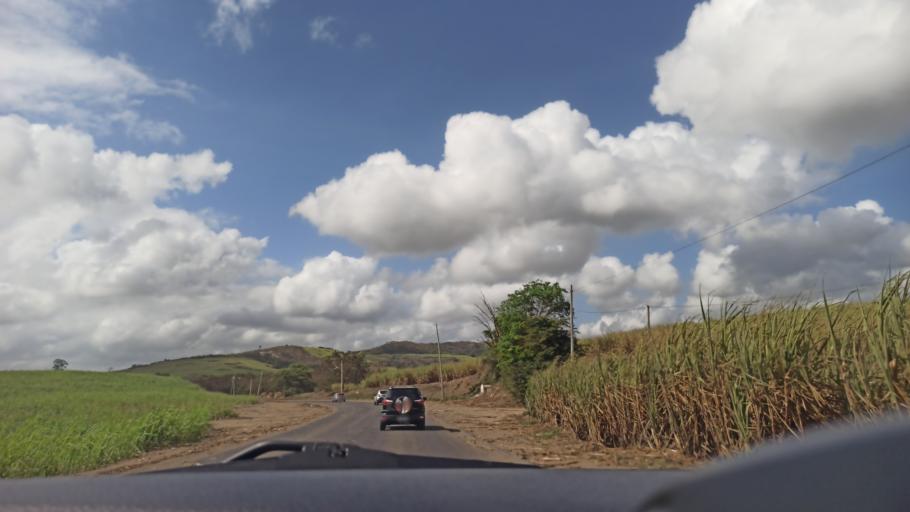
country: BR
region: Paraiba
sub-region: Juripiranga
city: Juripiranga
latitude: -7.4114
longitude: -35.2615
